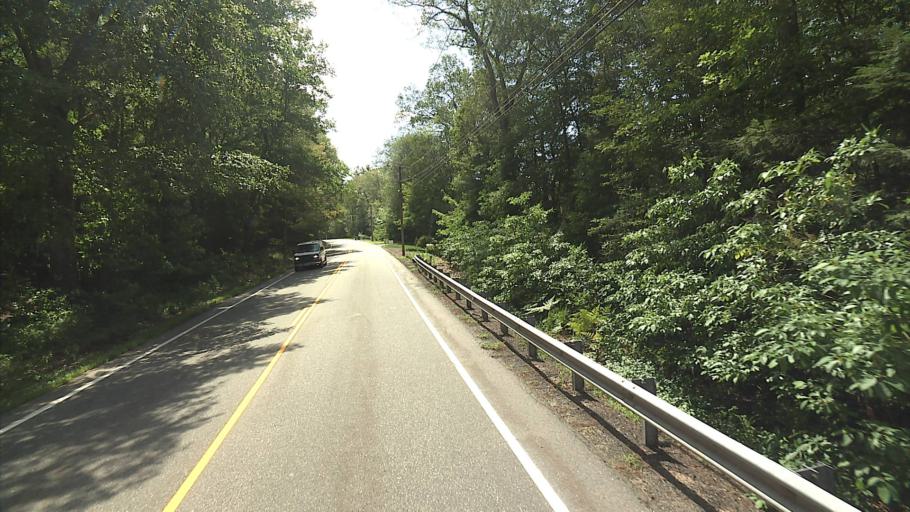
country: US
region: Massachusetts
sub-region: Worcester County
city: Southbridge
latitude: 41.9734
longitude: -72.0843
